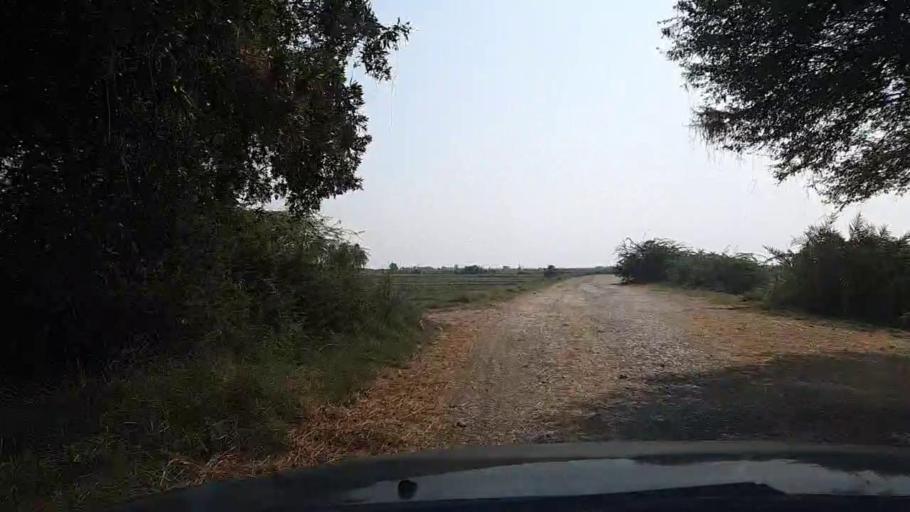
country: PK
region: Sindh
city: Mirpur Sakro
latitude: 24.3907
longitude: 67.6651
